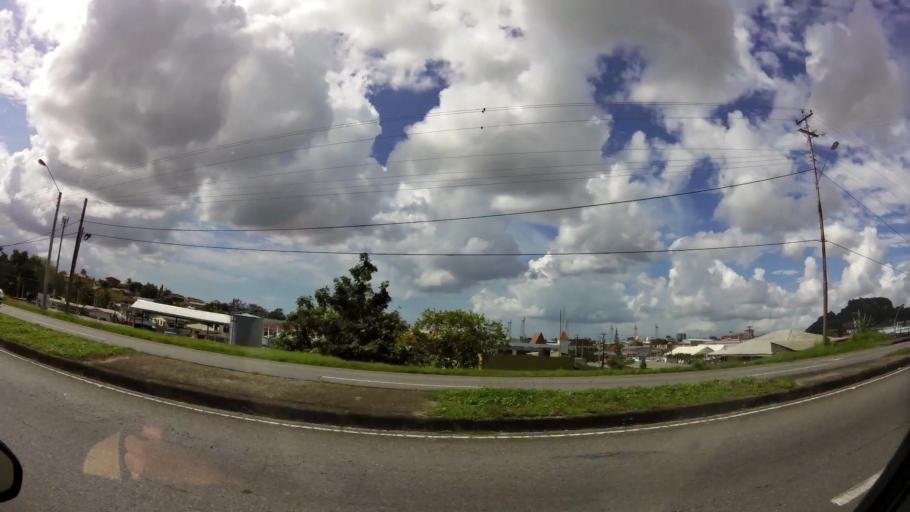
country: TT
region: City of San Fernando
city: Mon Repos
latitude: 10.2632
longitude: -61.4579
